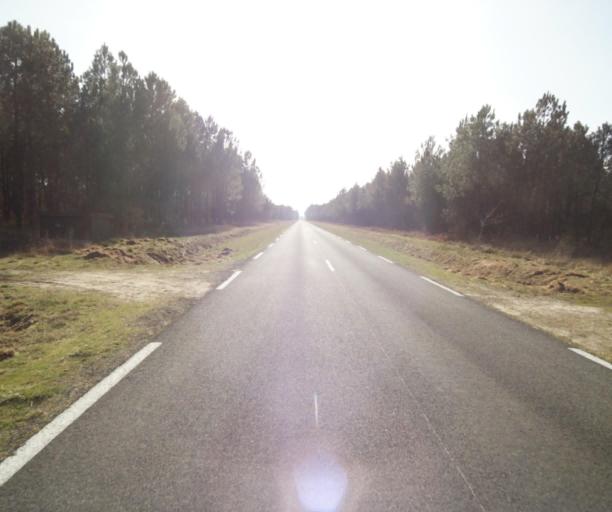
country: FR
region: Aquitaine
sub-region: Departement de la Gironde
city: Grignols
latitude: 44.1854
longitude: -0.1453
